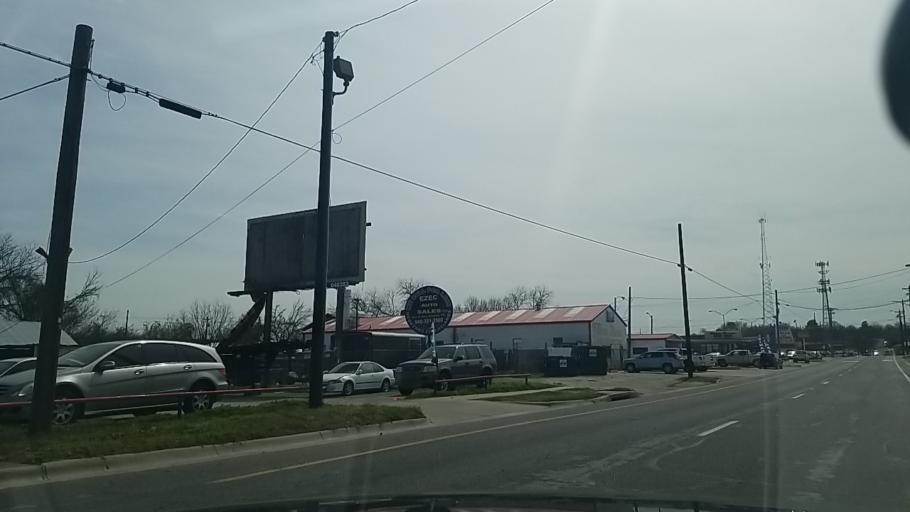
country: US
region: Texas
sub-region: Denton County
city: Denton
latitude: 33.2107
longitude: -97.1338
